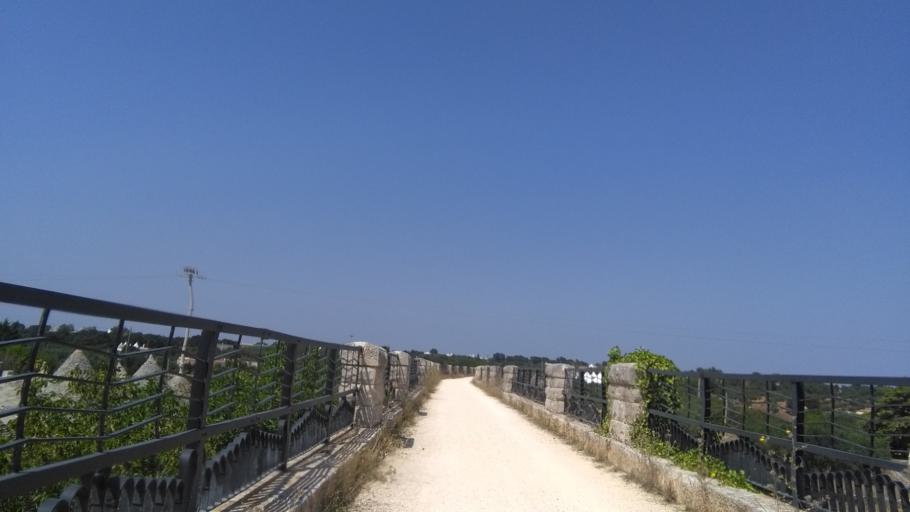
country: IT
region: Apulia
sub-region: Provincia di Brindisi
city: Cisternino
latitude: 40.6961
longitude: 17.4228
